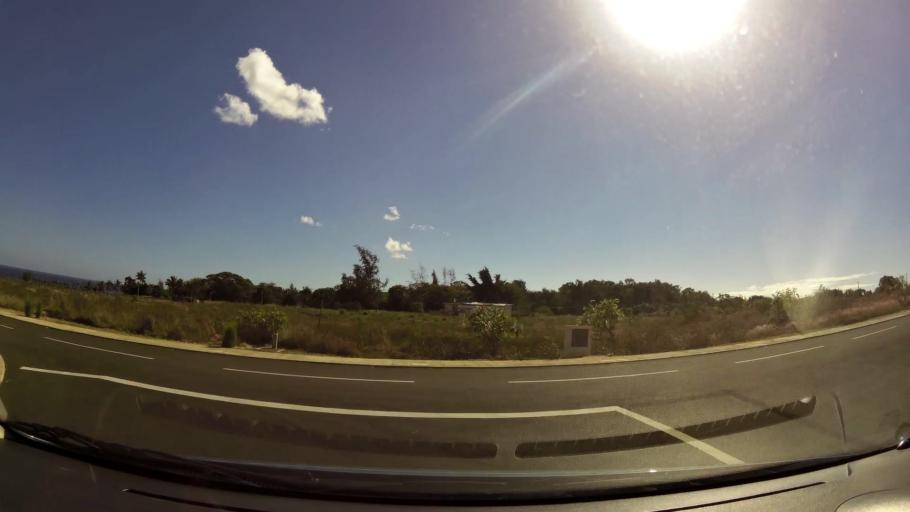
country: MU
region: Black River
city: Flic en Flac
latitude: -20.2689
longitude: 57.3858
